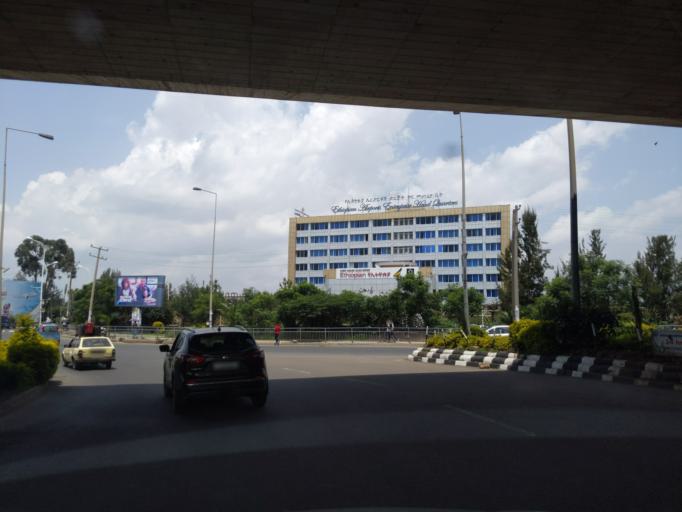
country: ET
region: Adis Abeba
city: Addis Ababa
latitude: 8.9873
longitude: 38.7911
